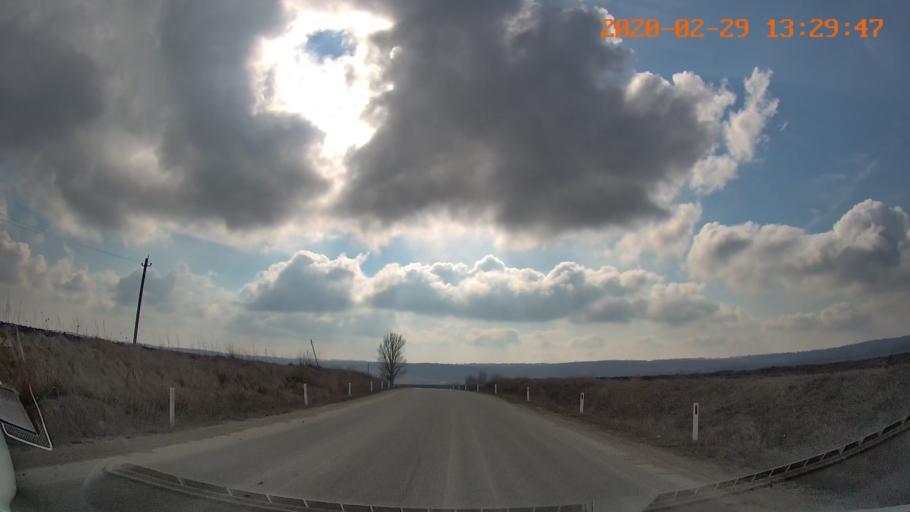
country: MD
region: Telenesti
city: Camenca
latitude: 47.8935
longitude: 28.6337
